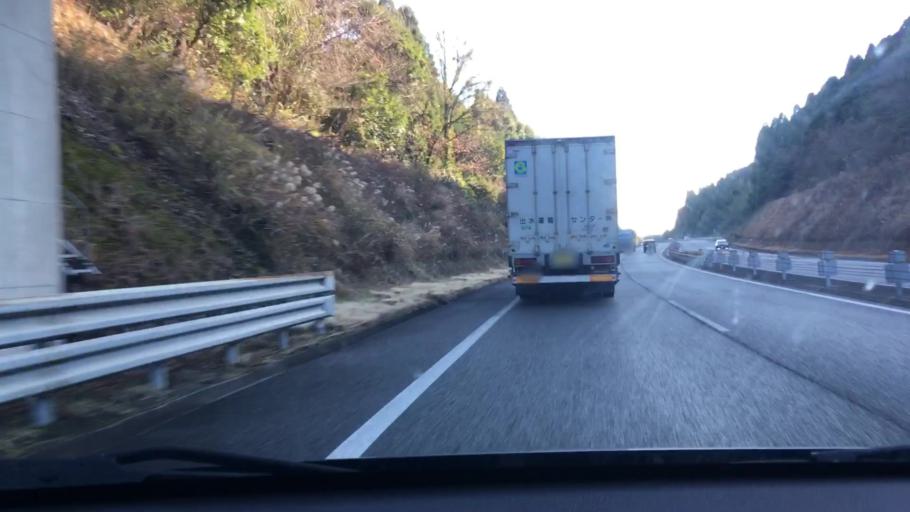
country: JP
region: Kagoshima
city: Kajiki
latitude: 31.8285
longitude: 130.6939
